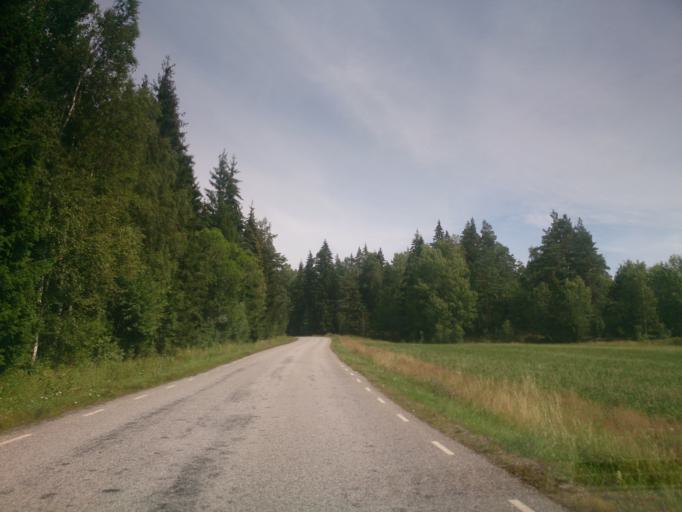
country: SE
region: OEstergoetland
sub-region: Valdemarsviks Kommun
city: Gusum
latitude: 58.3287
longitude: 16.5823
